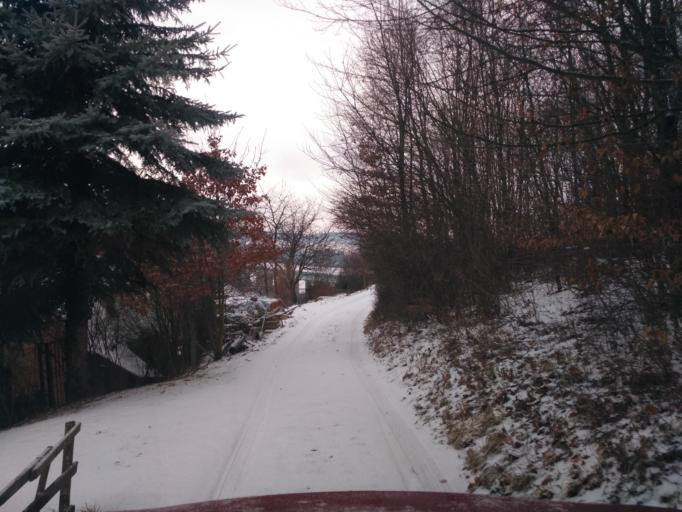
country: SK
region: Presovsky
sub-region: Okres Presov
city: Presov
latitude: 49.0004
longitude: 21.1685
